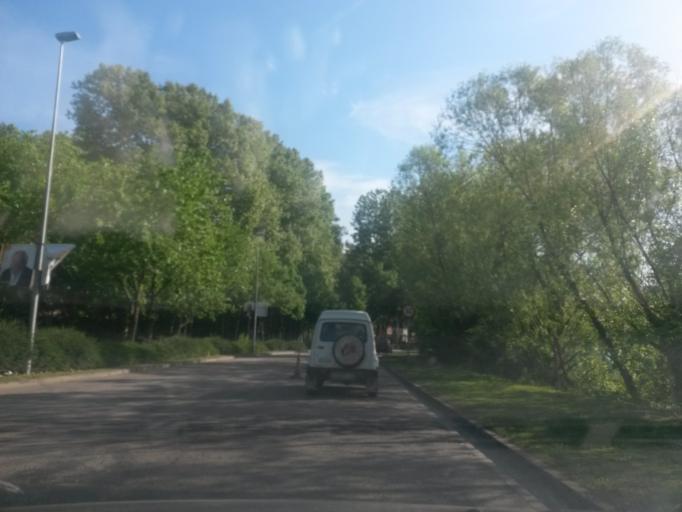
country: ES
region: Catalonia
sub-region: Provincia de Girona
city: Olot
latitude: 42.1740
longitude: 2.4877
